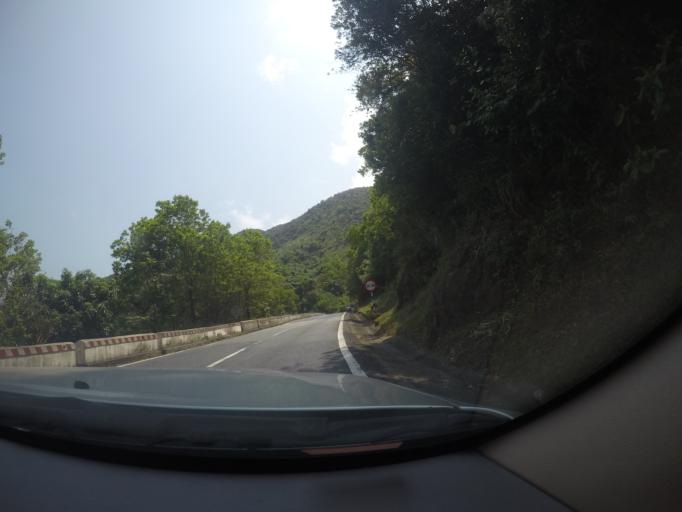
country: VN
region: Da Nang
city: Lien Chieu
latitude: 16.1955
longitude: 108.1219
